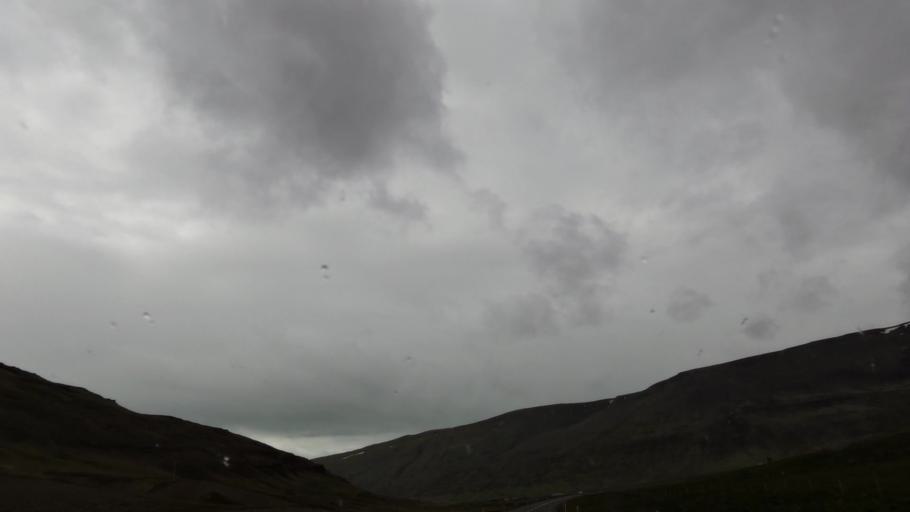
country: IS
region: West
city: Borgarnes
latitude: 65.3482
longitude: -21.7638
